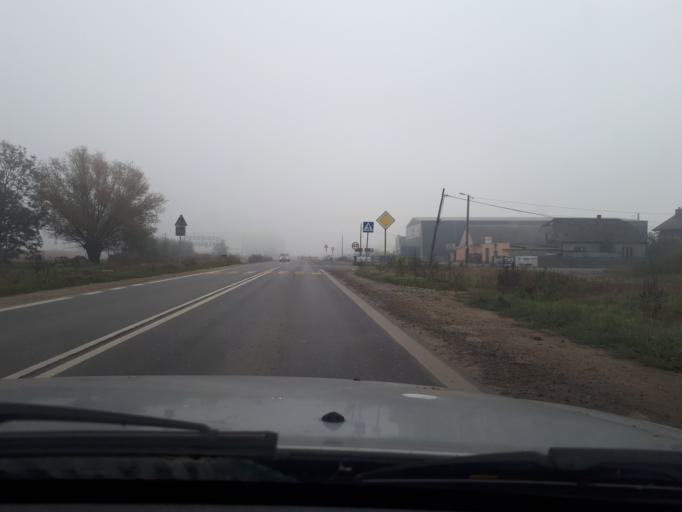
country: PL
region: Lesser Poland Voivodeship
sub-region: Powiat wielicki
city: Podleze
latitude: 50.0762
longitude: 20.1487
